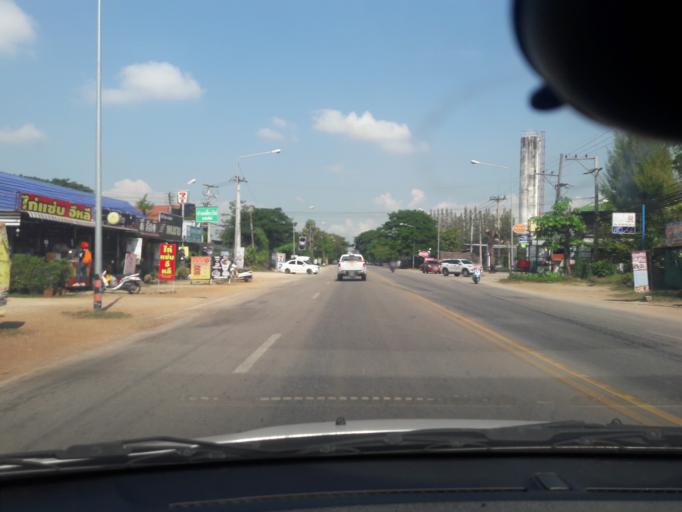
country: TH
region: Lampang
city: Lampang
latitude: 18.2436
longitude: 99.4912
